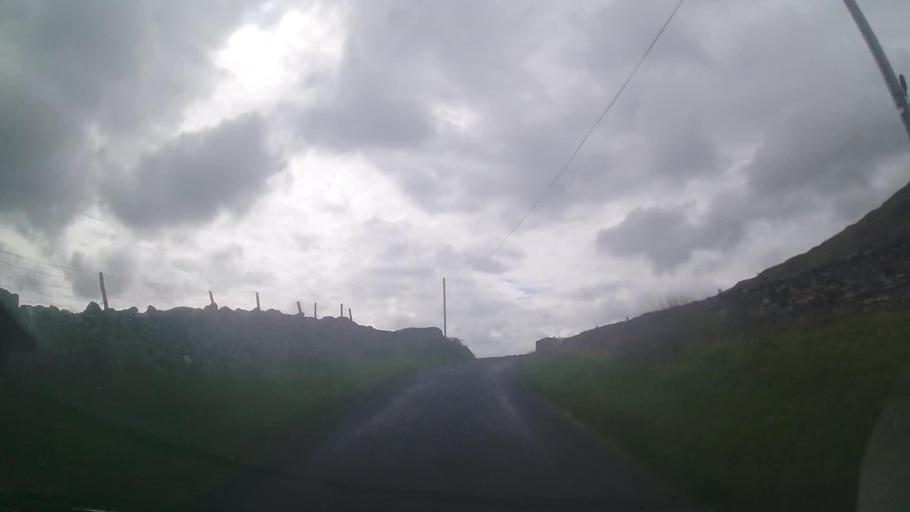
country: GB
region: England
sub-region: Cumbria
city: Ambleside
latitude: 54.4558
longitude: -2.9340
